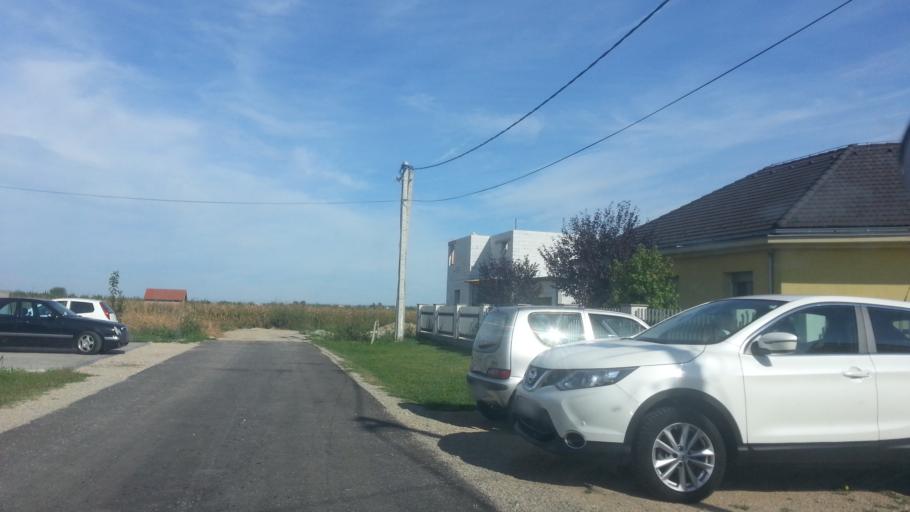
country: RS
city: Novi Banovci
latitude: 44.9702
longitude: 20.2715
